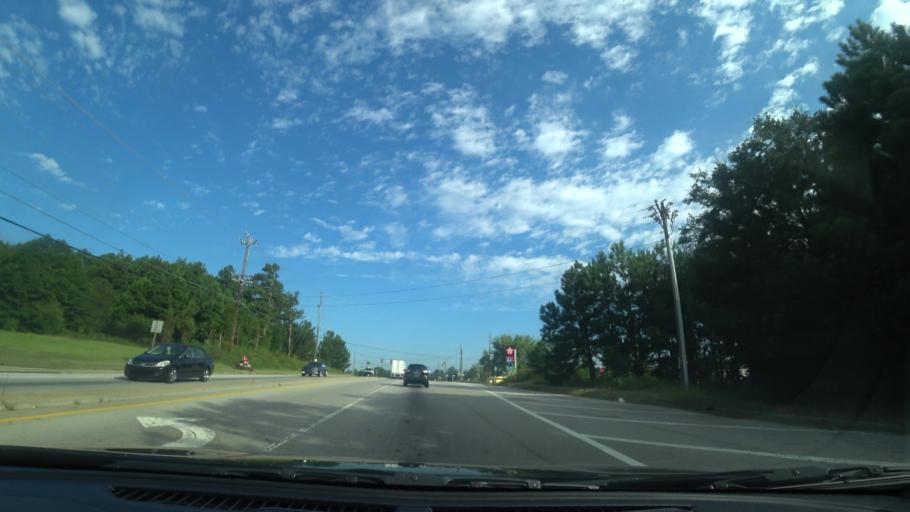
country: US
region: Georgia
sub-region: Rockdale County
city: Conyers
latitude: 33.6684
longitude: -83.9860
